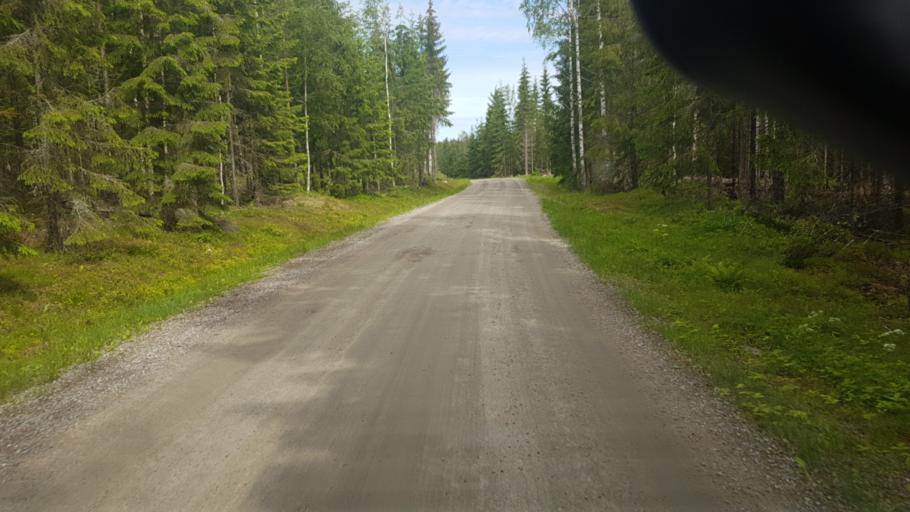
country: SE
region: Vaermland
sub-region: Eda Kommun
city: Amotfors
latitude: 59.8473
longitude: 12.5205
